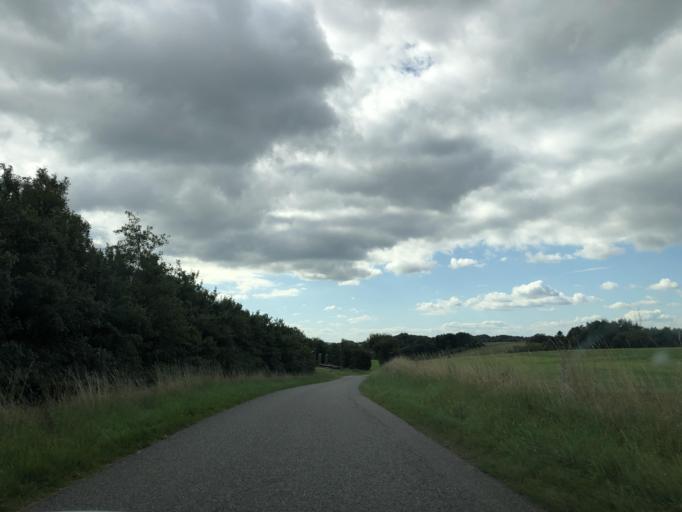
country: DK
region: North Denmark
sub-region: Vesthimmerland Kommune
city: Alestrup
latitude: 56.5906
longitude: 9.4045
